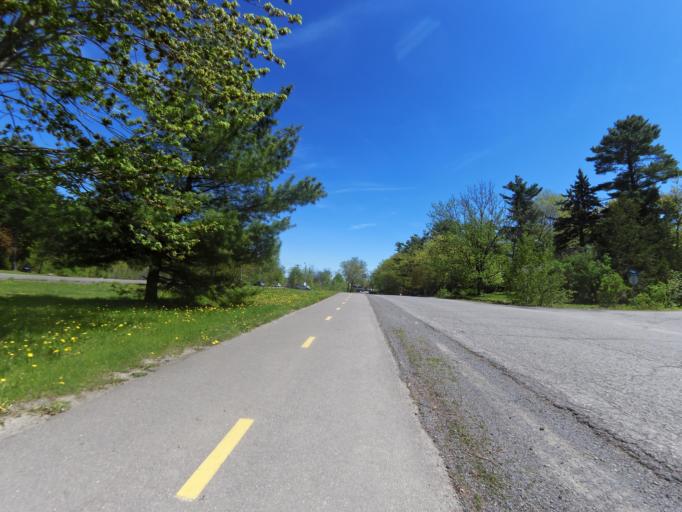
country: CA
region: Ontario
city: Bells Corners
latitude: 45.3877
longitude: -75.8380
